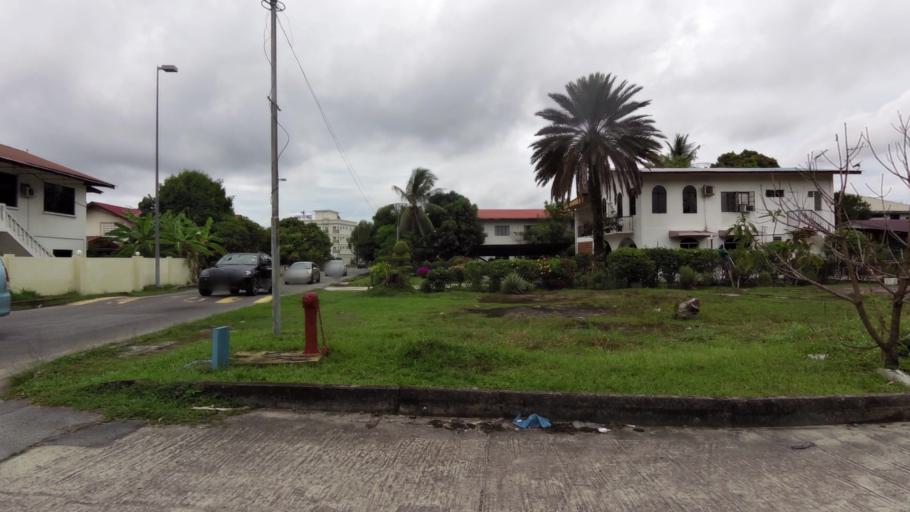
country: BN
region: Brunei and Muara
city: Bandar Seri Begawan
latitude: 4.8949
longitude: 114.9169
